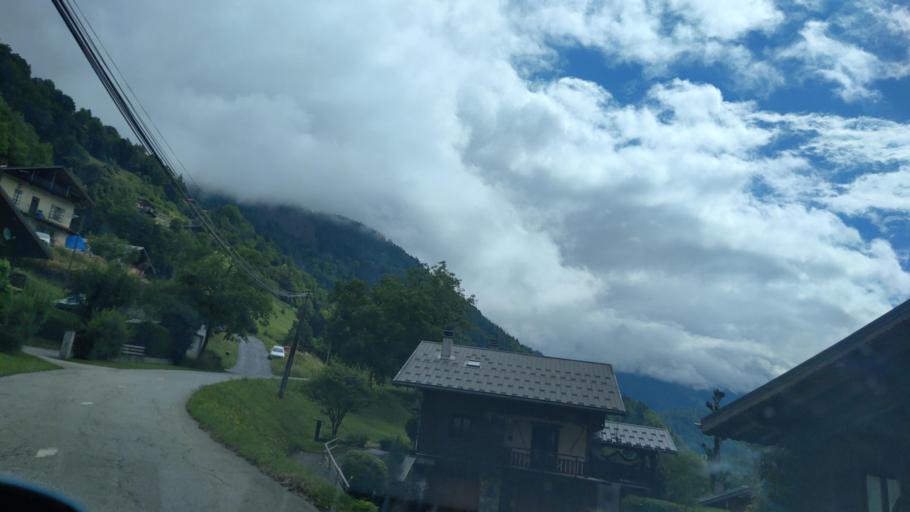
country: FR
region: Rhone-Alpes
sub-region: Departement de la Savoie
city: Beaufort
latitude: 45.7276
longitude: 6.5269
